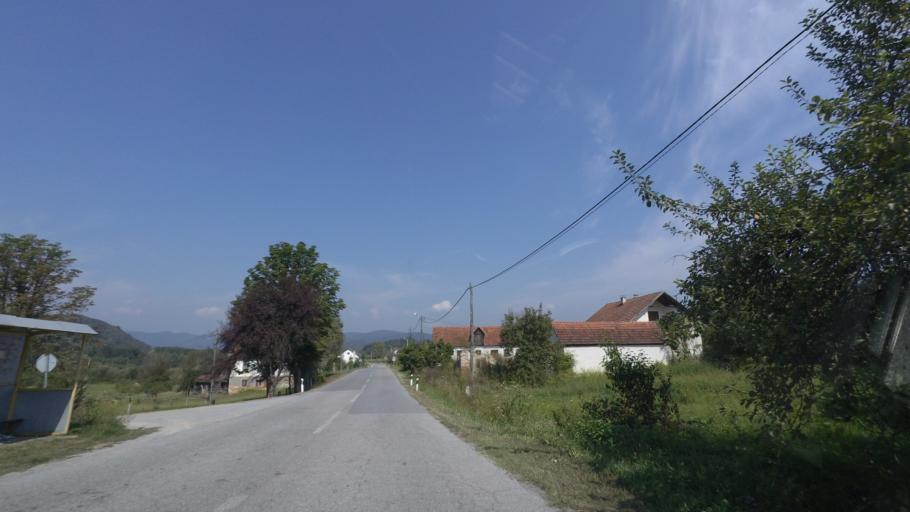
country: HR
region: Sisacko-Moslavacka
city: Dvor
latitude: 45.1052
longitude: 16.2871
